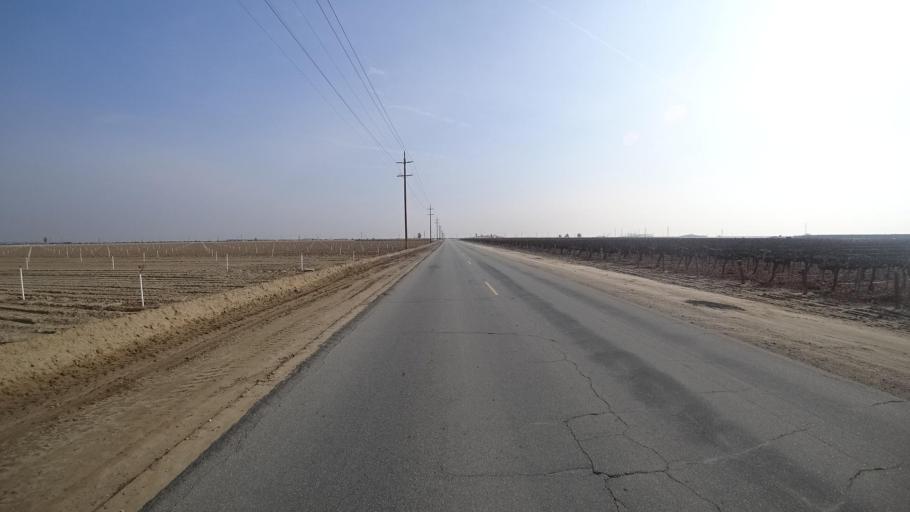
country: US
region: California
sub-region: Kern County
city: Weedpatch
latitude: 35.0965
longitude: -118.9908
